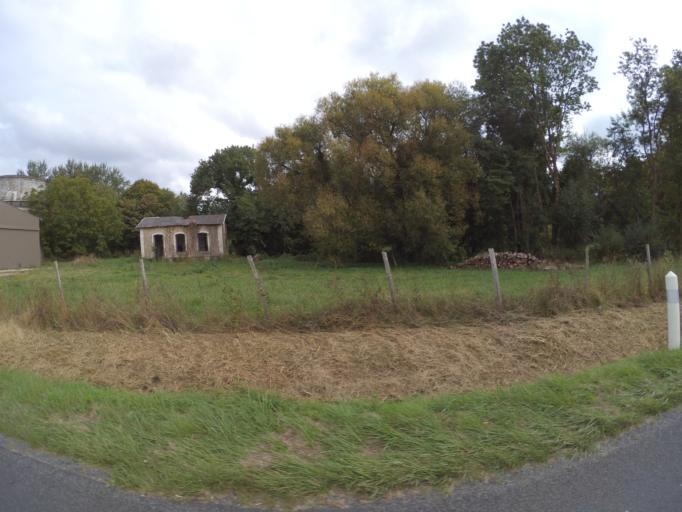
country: FR
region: Centre
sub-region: Departement d'Indre-et-Loire
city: Reugny
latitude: 47.4571
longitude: 0.8775
